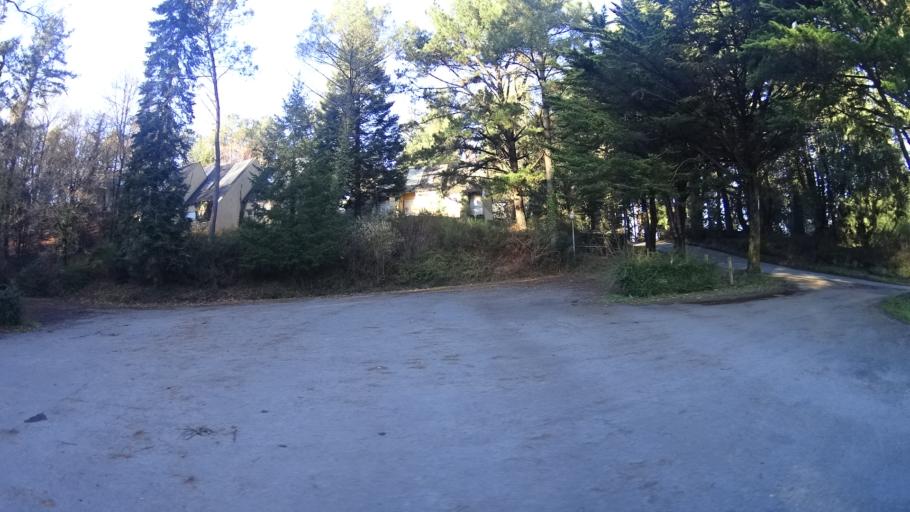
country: FR
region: Brittany
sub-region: Departement du Morbihan
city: Saint-Jacut-les-Pins
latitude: 47.6641
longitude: -2.1889
